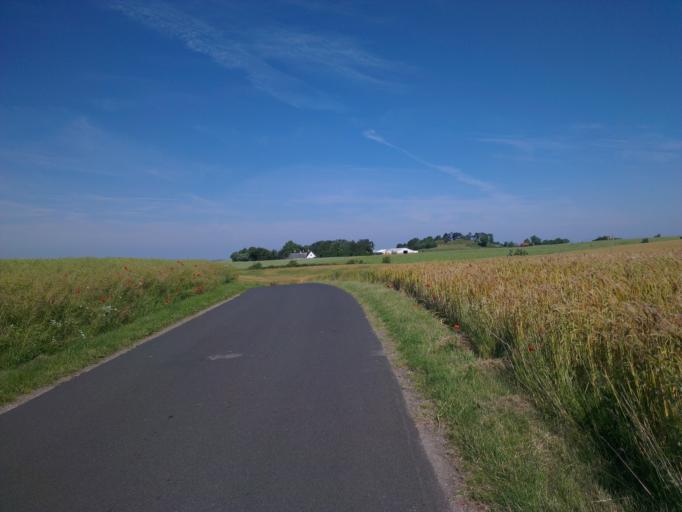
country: DK
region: Capital Region
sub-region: Frederikssund Kommune
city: Skibby
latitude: 55.7805
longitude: 11.8959
